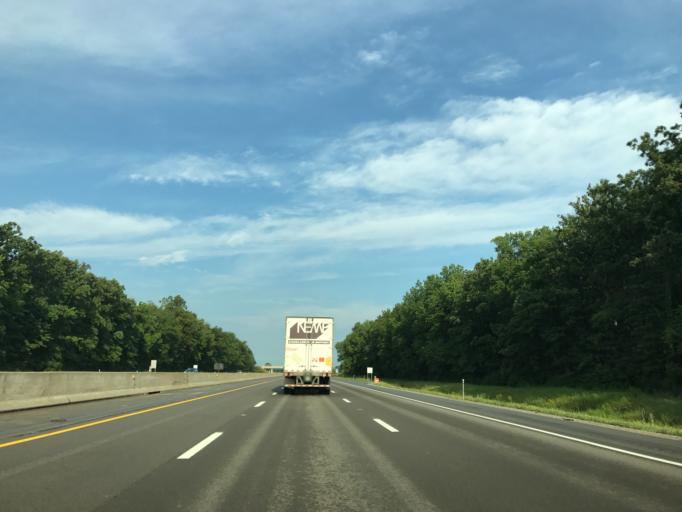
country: US
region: Ohio
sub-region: Sandusky County
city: Clyde
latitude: 41.3595
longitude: -82.9095
